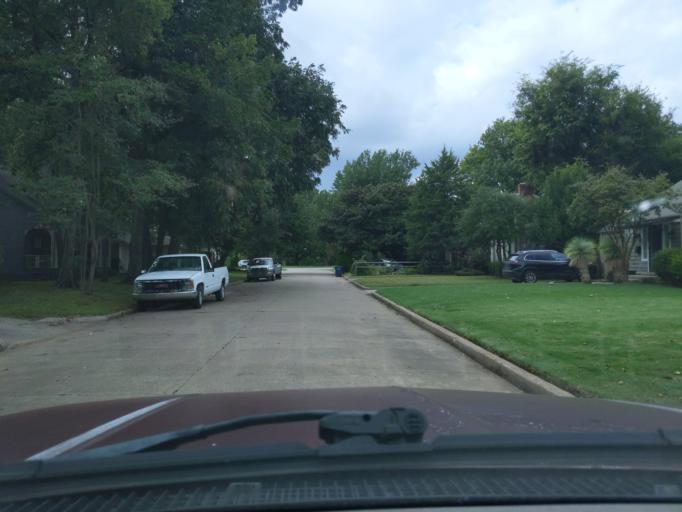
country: US
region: Oklahoma
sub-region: Tulsa County
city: Tulsa
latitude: 36.1107
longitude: -95.9824
